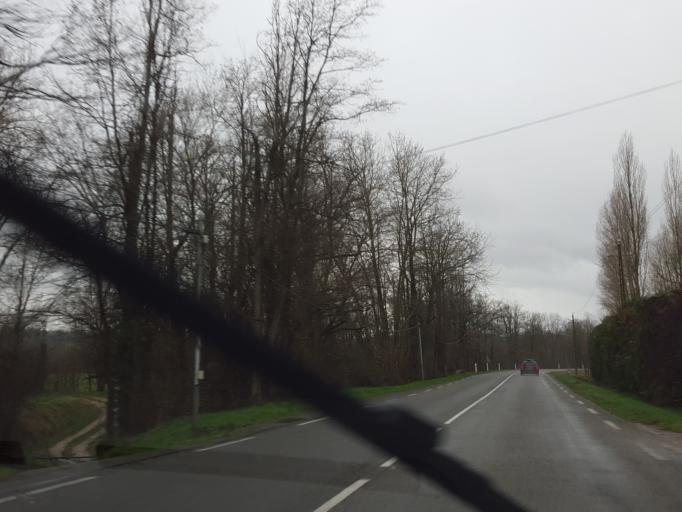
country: FR
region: Midi-Pyrenees
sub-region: Departement de l'Ariege
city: Mirepoix
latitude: 43.0973
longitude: 1.8979
